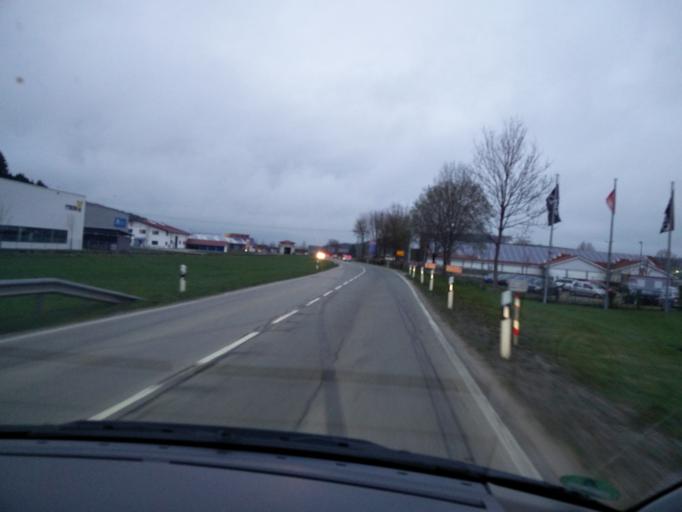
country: DE
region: Bavaria
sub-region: Upper Bavaria
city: Bad Endorf
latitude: 47.9175
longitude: 12.2927
